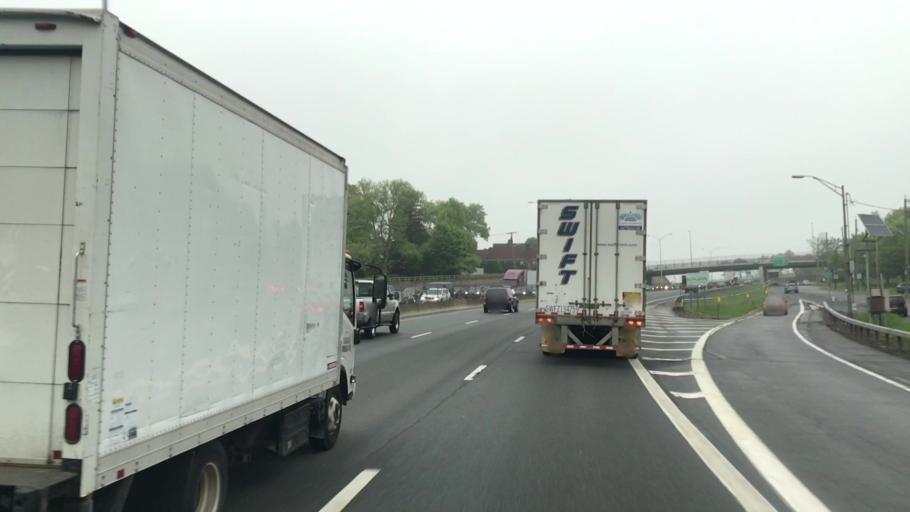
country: US
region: New York
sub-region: Westchester County
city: Yonkers
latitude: 40.9103
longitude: -73.8770
